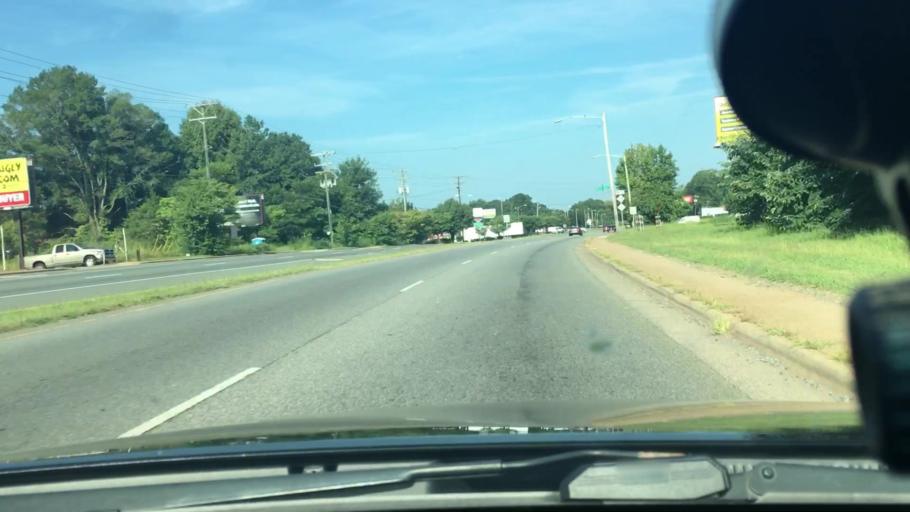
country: US
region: North Carolina
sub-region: Mecklenburg County
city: Mint Hill
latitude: 35.2085
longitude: -80.6705
